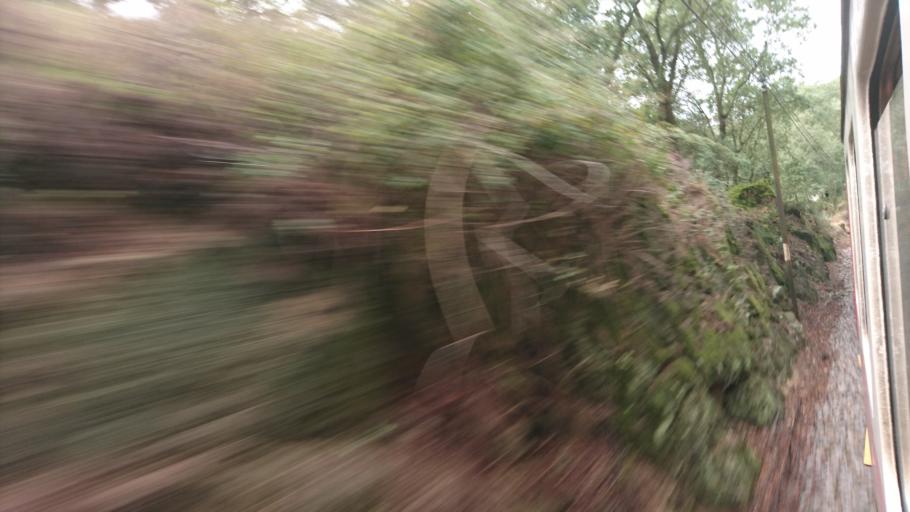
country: PT
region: Viseu
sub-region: Cinfaes
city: Cinfaes
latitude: 41.0936
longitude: -8.0635
